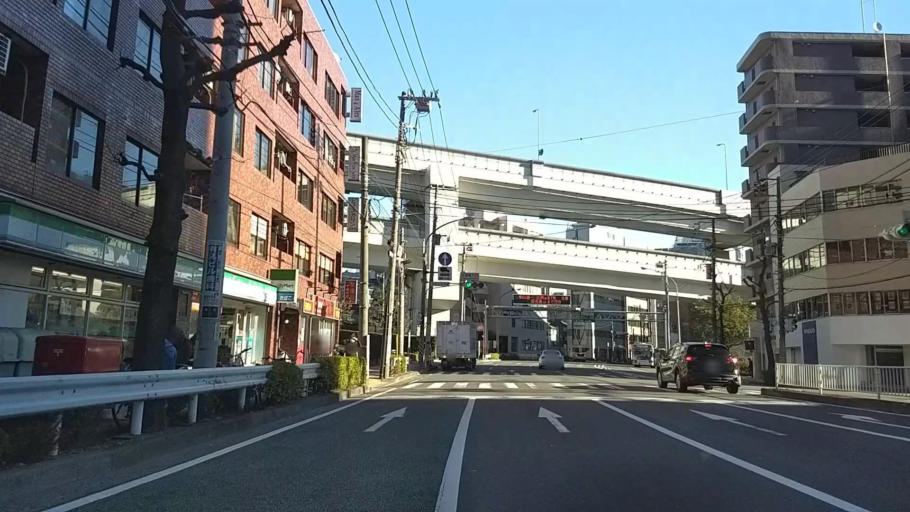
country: JP
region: Kanagawa
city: Yokohama
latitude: 35.4684
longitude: 139.6144
